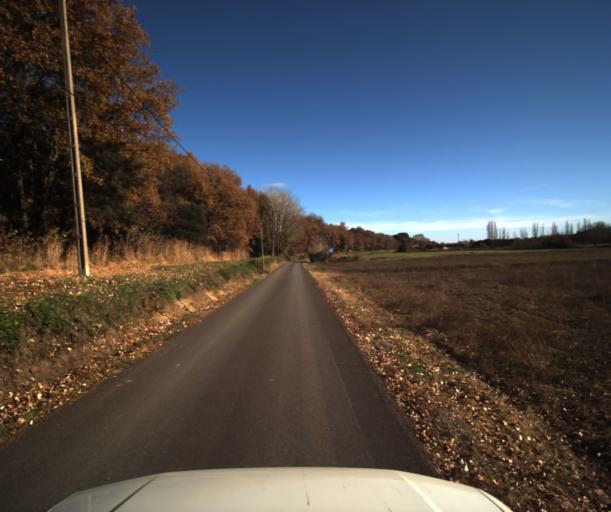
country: FR
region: Provence-Alpes-Cote d'Azur
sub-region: Departement du Vaucluse
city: Pertuis
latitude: 43.6971
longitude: 5.4718
